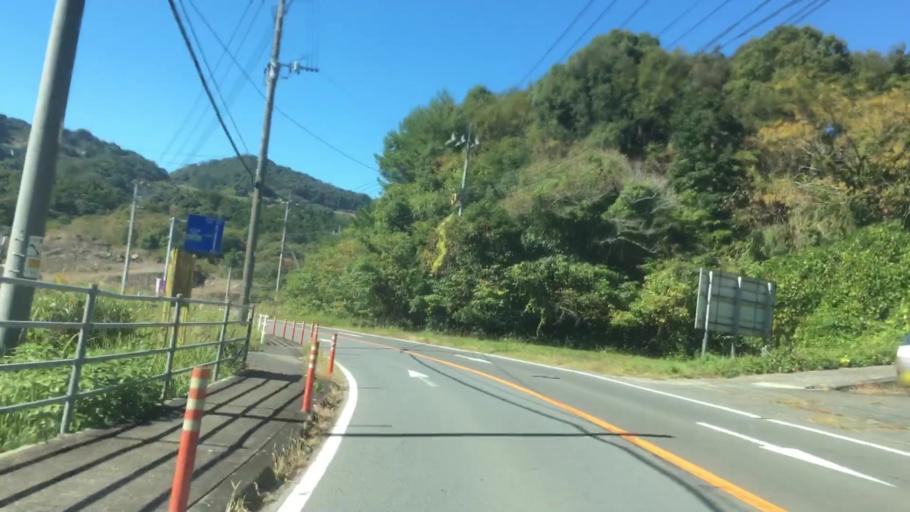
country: JP
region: Nagasaki
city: Sasebo
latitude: 32.9935
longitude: 129.7349
